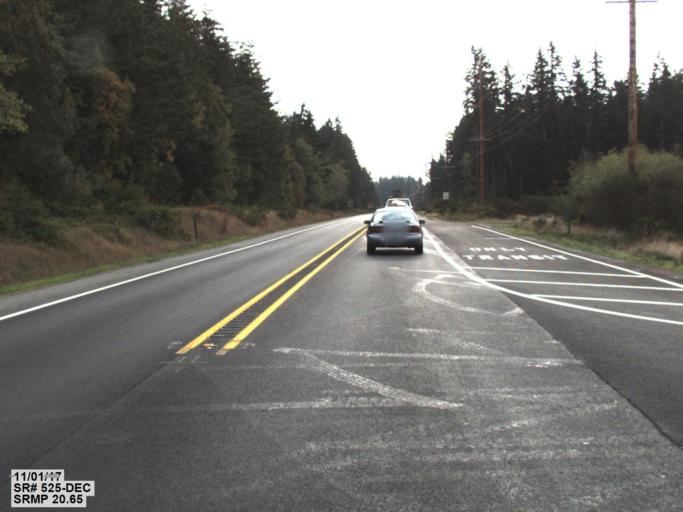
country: US
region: Washington
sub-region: Island County
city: Freeland
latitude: 48.0355
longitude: -122.5640
